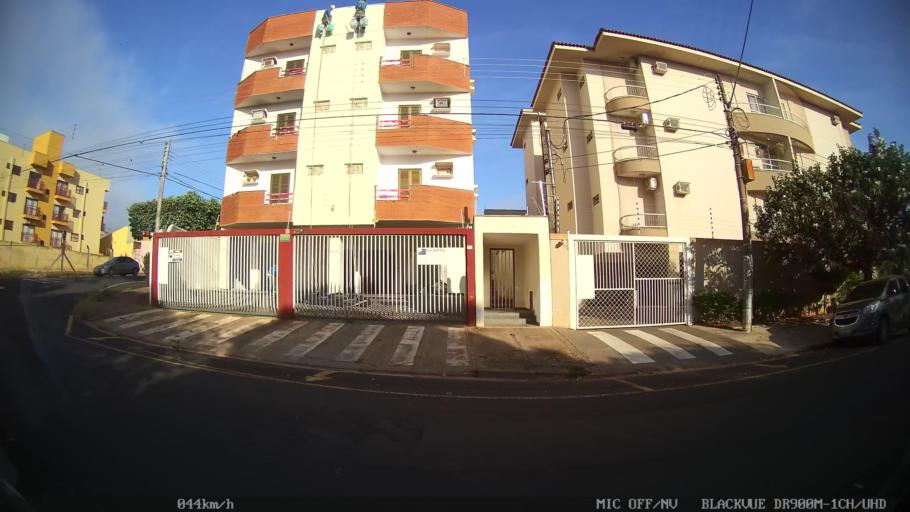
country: BR
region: Sao Paulo
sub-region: Sao Jose Do Rio Preto
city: Sao Jose do Rio Preto
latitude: -20.8321
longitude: -49.3661
